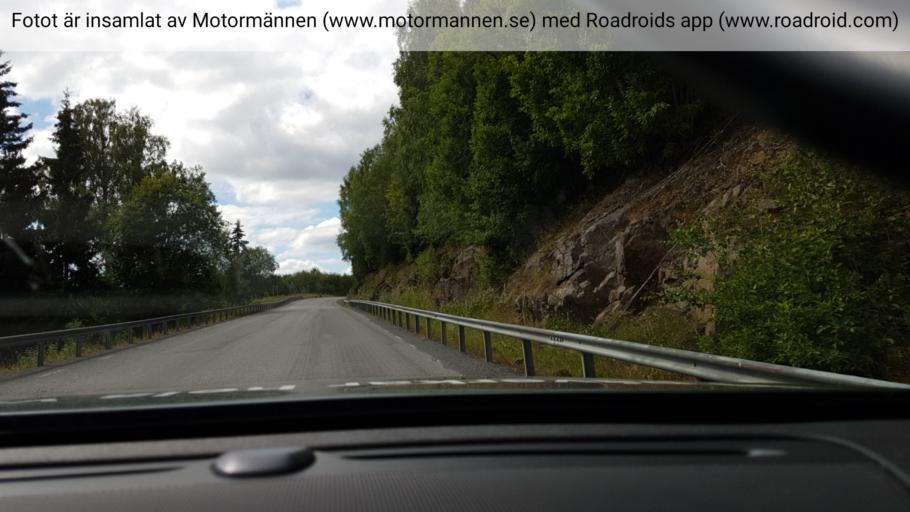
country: SE
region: Vaesternorrland
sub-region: Kramfors Kommun
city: Nordingra
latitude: 62.9412
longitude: 18.2457
